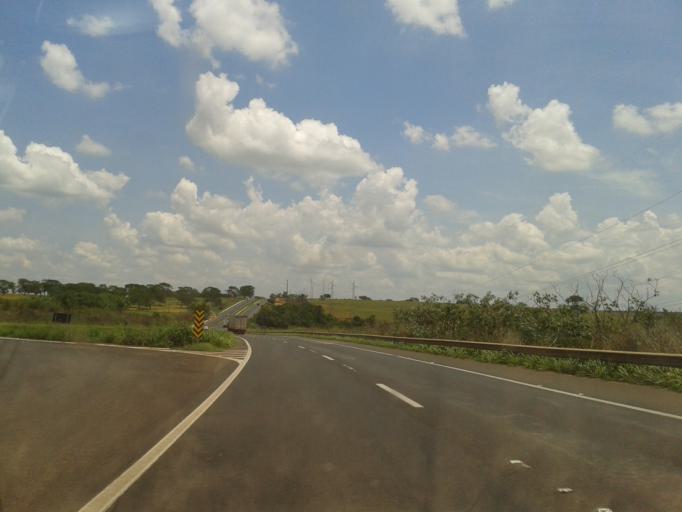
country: BR
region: Minas Gerais
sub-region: Uberlandia
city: Uberlandia
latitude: -18.8671
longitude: -48.5680
